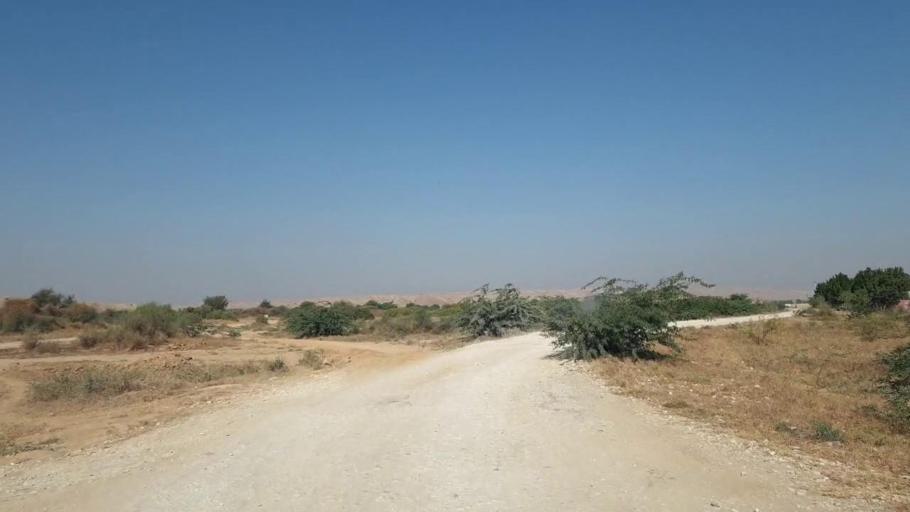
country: PK
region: Sindh
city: Gharo
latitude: 25.1703
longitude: 67.7332
